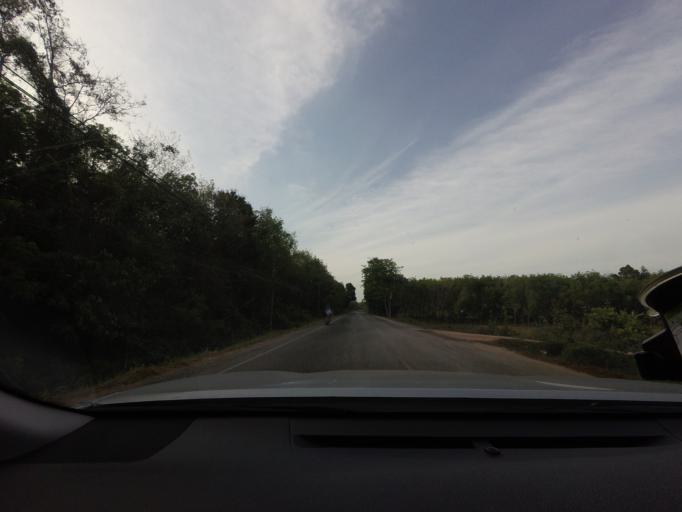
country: TH
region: Narathiwat
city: Ra-ngae
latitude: 6.3259
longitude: 101.7262
